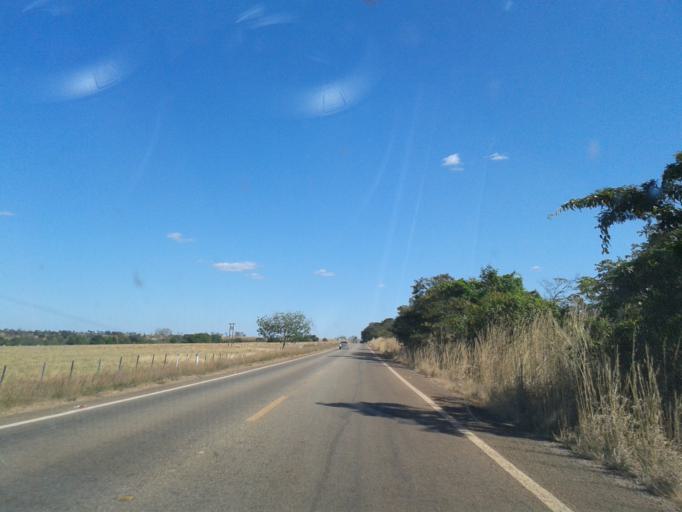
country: BR
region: Goias
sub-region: Mozarlandia
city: Mozarlandia
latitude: -14.3701
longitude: -50.4303
